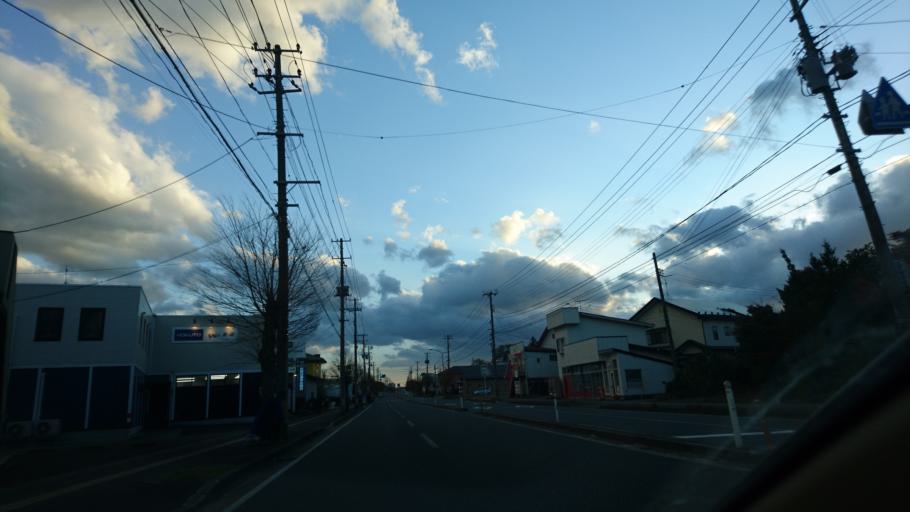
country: JP
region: Iwate
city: Mizusawa
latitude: 39.1498
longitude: 141.1323
